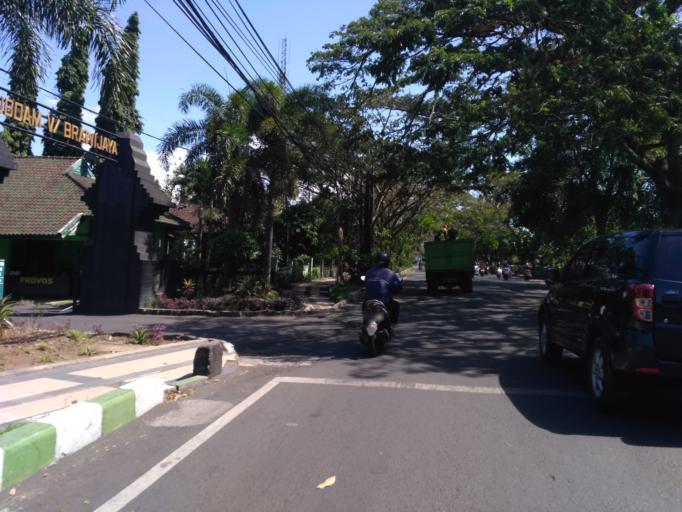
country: ID
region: East Java
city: Malang
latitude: -7.9784
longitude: 112.6453
